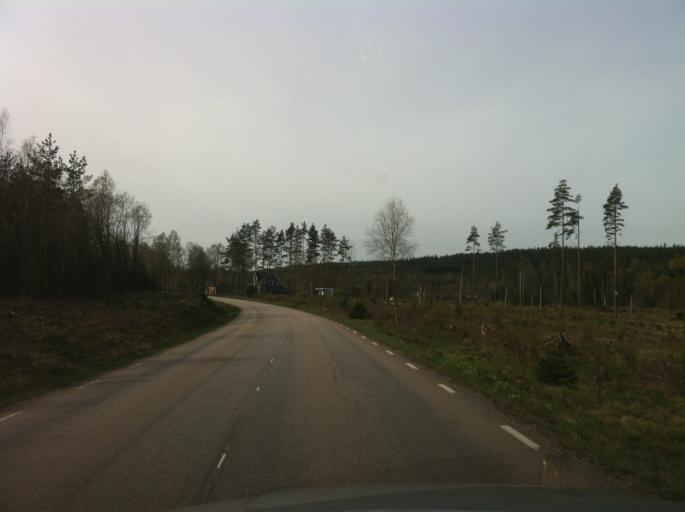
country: SE
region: Vaestra Goetaland
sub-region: Bollebygds Kommun
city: Bollebygd
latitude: 57.7243
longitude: 12.5864
